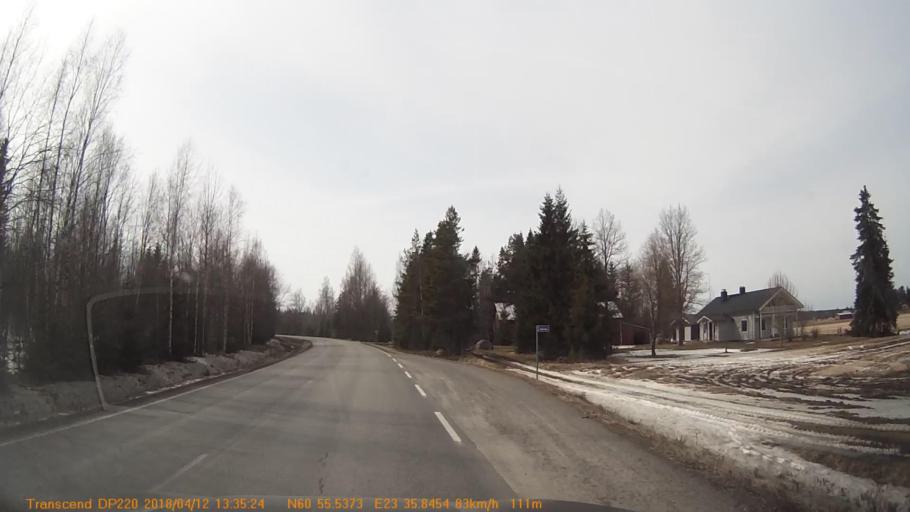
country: FI
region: Haeme
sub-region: Forssa
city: Forssa
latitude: 60.9255
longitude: 23.5968
